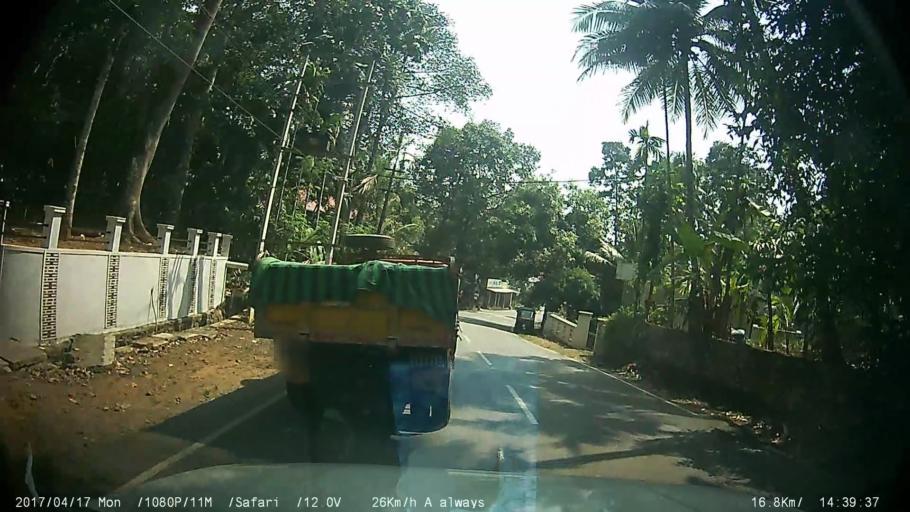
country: IN
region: Kerala
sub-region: Ernakulam
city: Piravam
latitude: 9.8337
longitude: 76.5162
